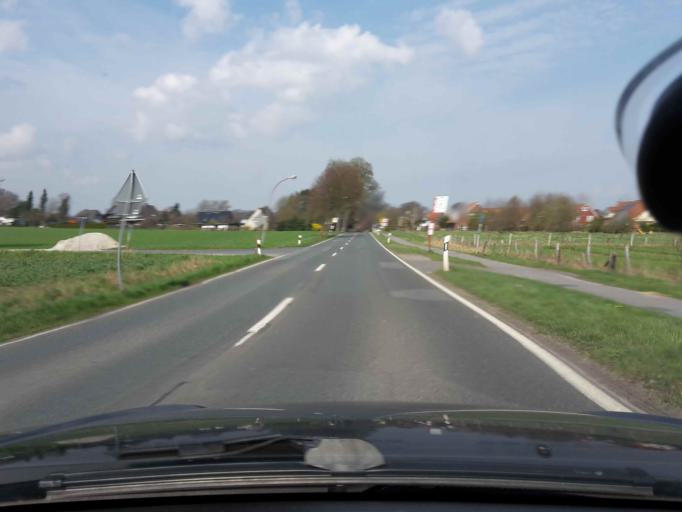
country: DE
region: Lower Saxony
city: Harmstorf
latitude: 53.3602
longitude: 9.9873
